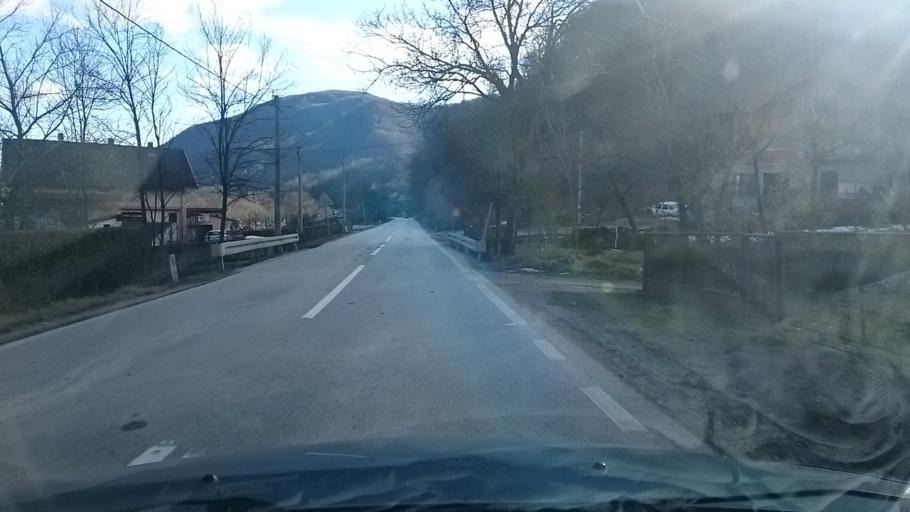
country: BA
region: Republika Srpska
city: Hiseti
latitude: 44.7170
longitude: 17.1639
